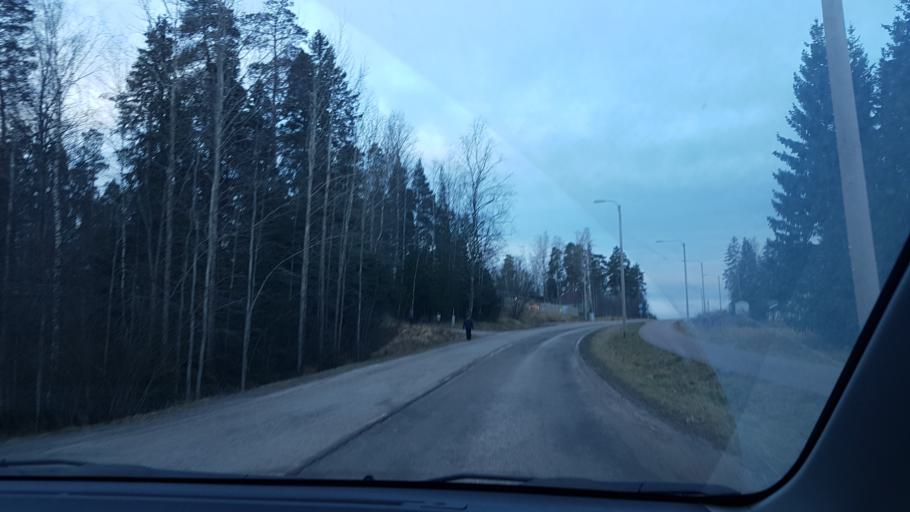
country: FI
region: Uusimaa
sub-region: Helsinki
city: Nurmijaervi
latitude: 60.3657
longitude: 24.7511
